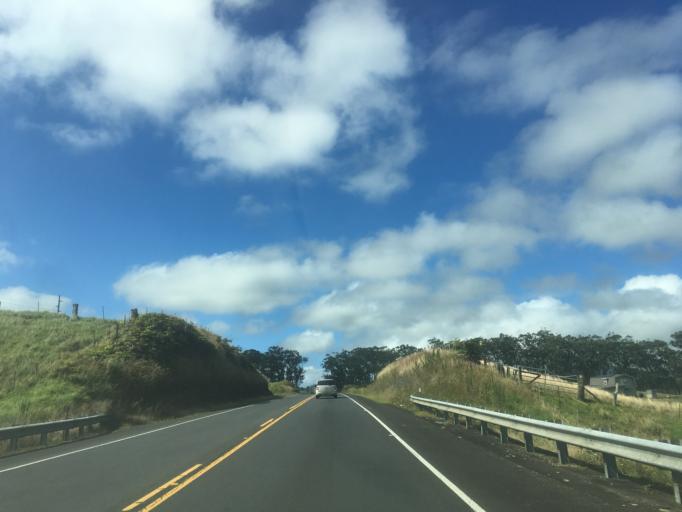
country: US
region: Hawaii
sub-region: Hawaii County
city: Honoka'a
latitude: 20.0500
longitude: -155.5687
